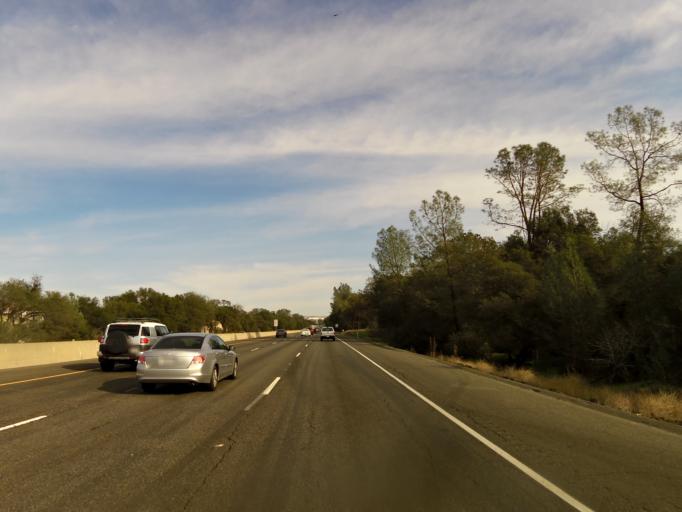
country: US
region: California
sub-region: Sacramento County
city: Folsom
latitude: 38.6405
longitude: -121.1919
